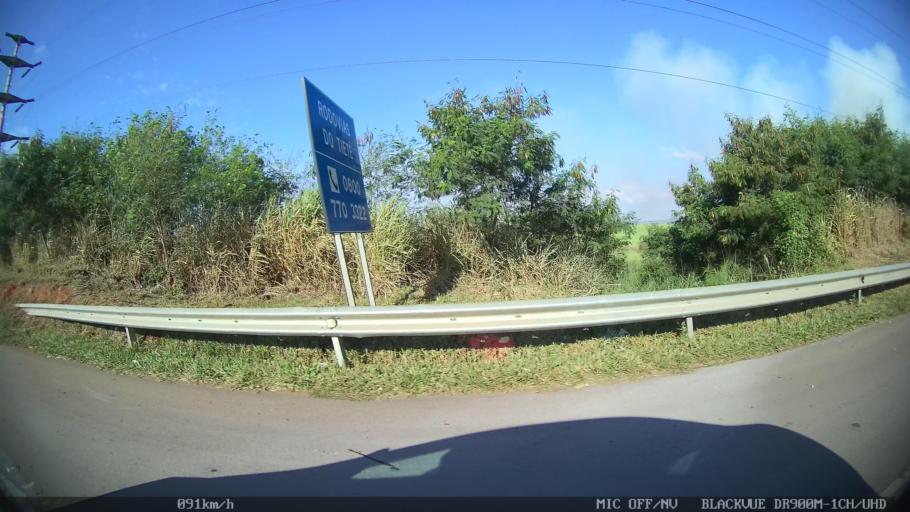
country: BR
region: Sao Paulo
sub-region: Piracicaba
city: Piracicaba
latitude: -22.6854
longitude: -47.5966
